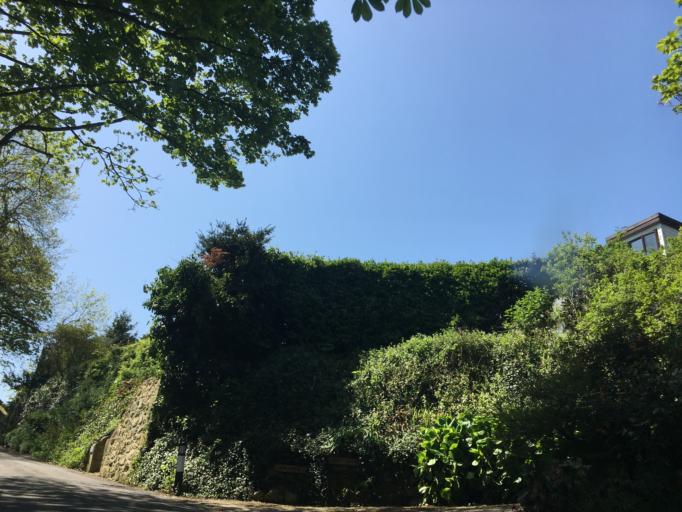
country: GB
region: England
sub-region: Isle of Wight
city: Ventnor
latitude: 50.5878
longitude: -1.2419
